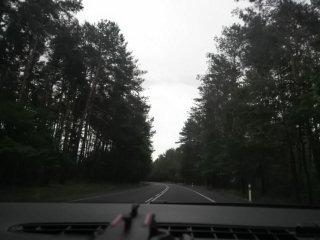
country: PL
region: Lublin Voivodeship
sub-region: Powiat janowski
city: Janow Lubelski
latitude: 50.6907
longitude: 22.3711
